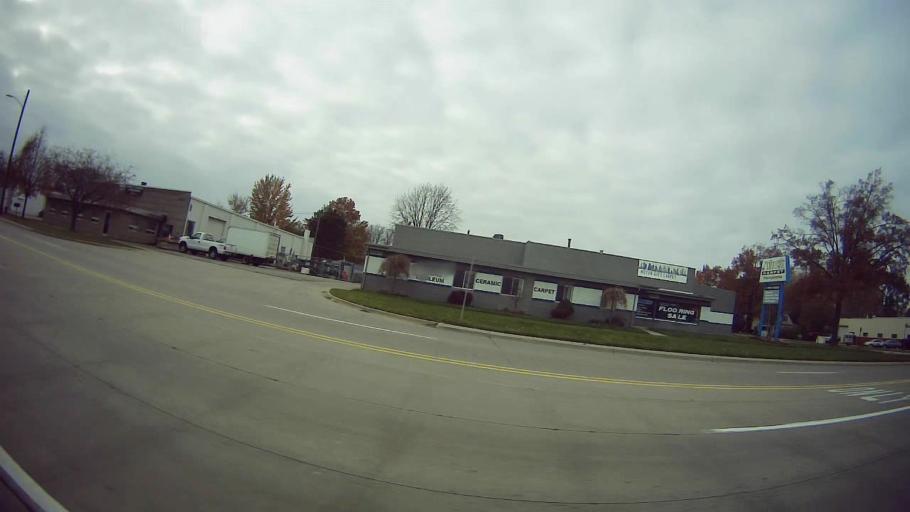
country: US
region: Michigan
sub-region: Macomb County
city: Warren
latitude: 42.4694
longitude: -83.0647
